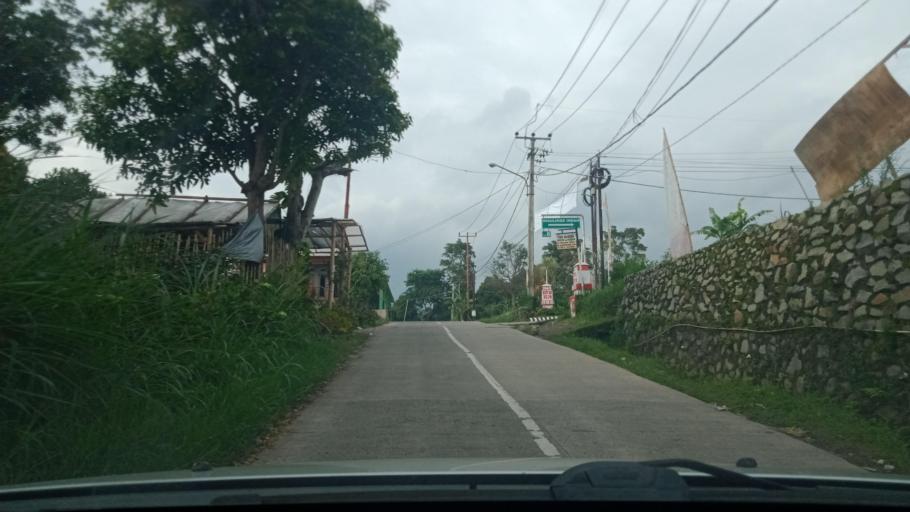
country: ID
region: West Java
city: Lembang
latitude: -6.8209
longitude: 107.5757
